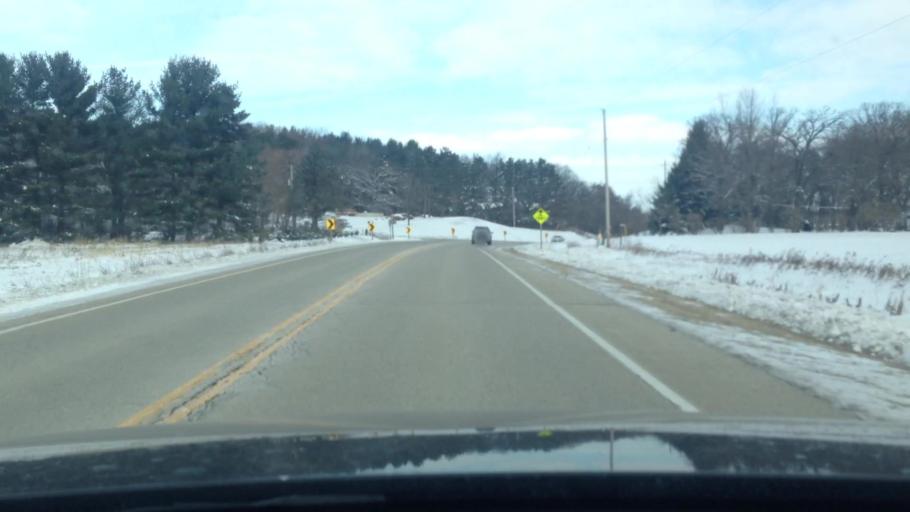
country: US
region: Wisconsin
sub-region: Walworth County
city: Lake Geneva
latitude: 42.6304
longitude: -88.4137
